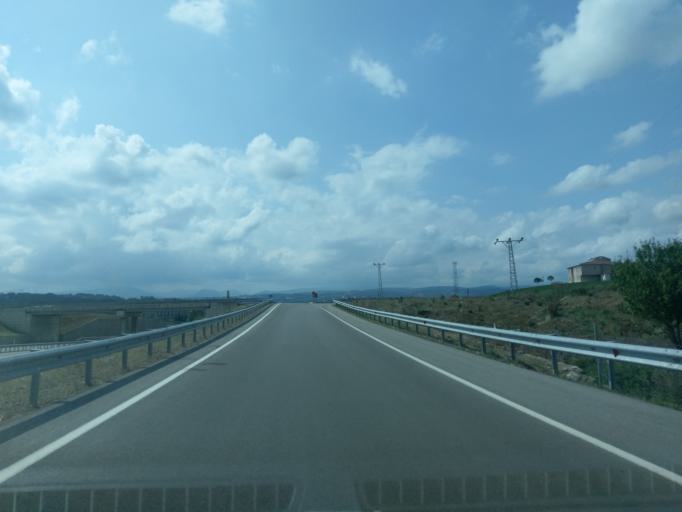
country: TR
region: Sinop
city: Kabali
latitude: 41.9291
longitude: 35.0842
